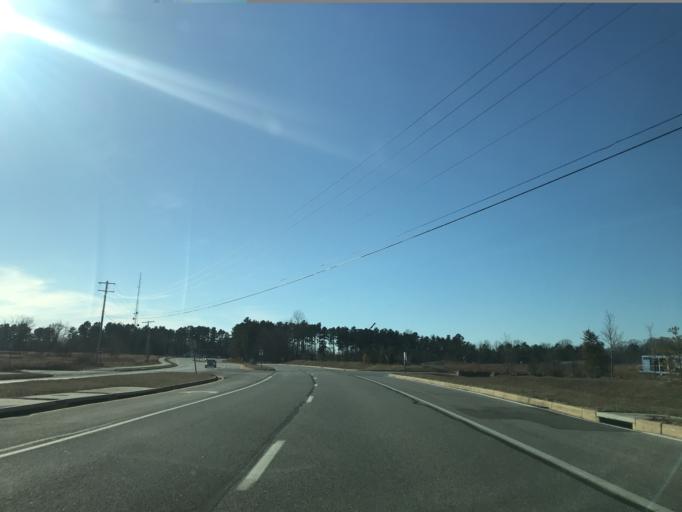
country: US
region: Maryland
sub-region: Charles County
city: La Plata
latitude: 38.5586
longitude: -76.9738
